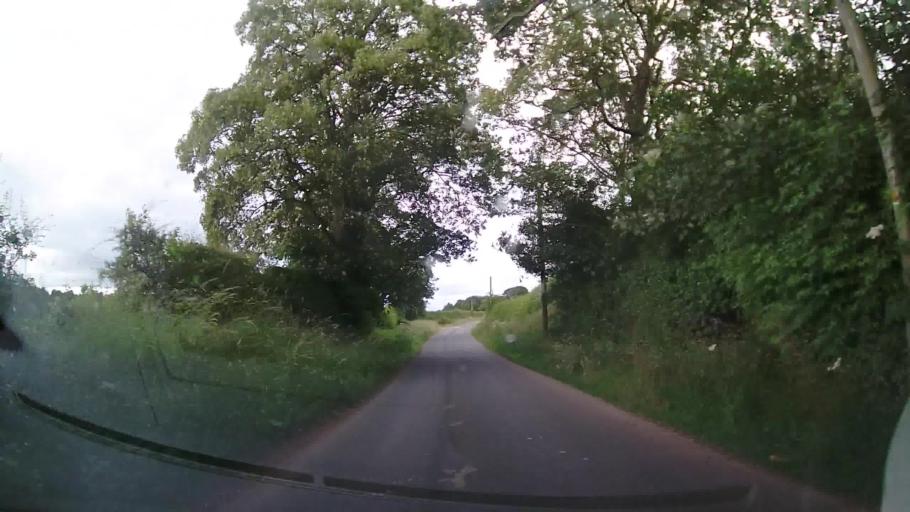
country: GB
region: England
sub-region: Shropshire
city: Whitchurch
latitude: 52.9288
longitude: -2.7318
